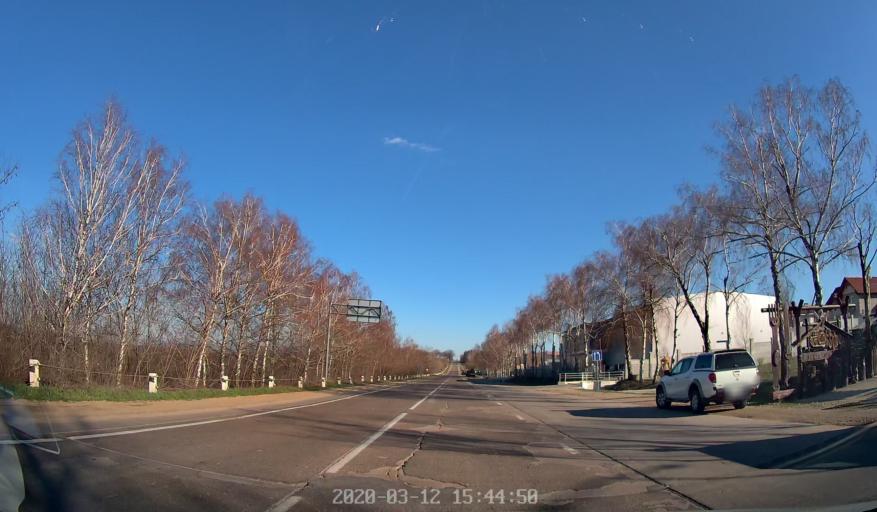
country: MD
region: Chisinau
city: Stauceni
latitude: 47.1092
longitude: 28.8664
